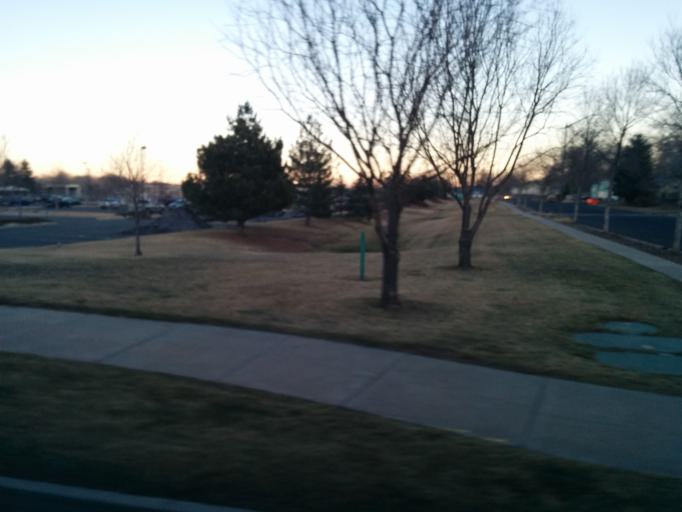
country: US
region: Colorado
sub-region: Larimer County
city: Fort Collins
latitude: 40.5952
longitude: -105.0910
